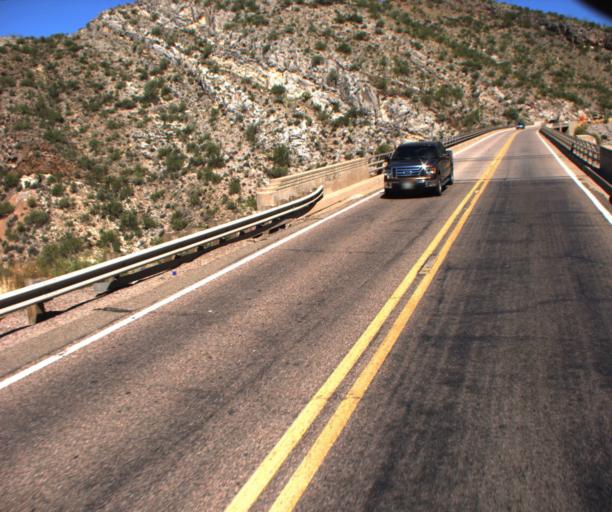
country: US
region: Arizona
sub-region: Pinal County
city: Superior
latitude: 33.2980
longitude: -111.0893
